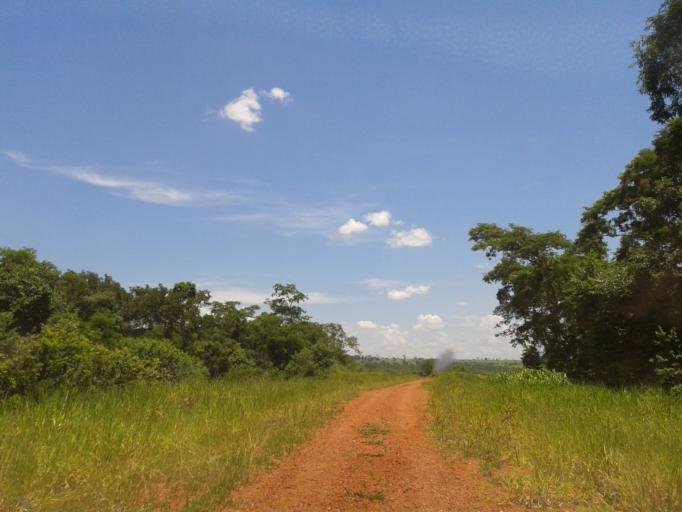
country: BR
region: Minas Gerais
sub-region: Santa Vitoria
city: Santa Vitoria
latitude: -19.1420
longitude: -50.5714
